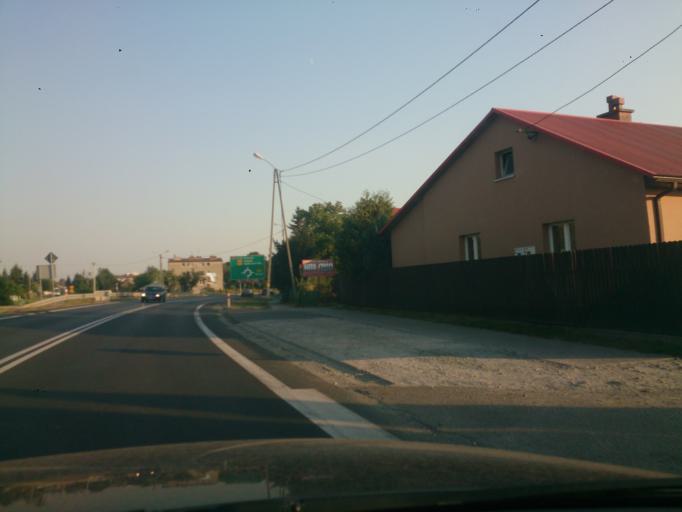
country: PL
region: Subcarpathian Voivodeship
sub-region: Powiat kolbuszowski
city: Kolbuszowa
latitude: 50.2527
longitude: 21.7727
